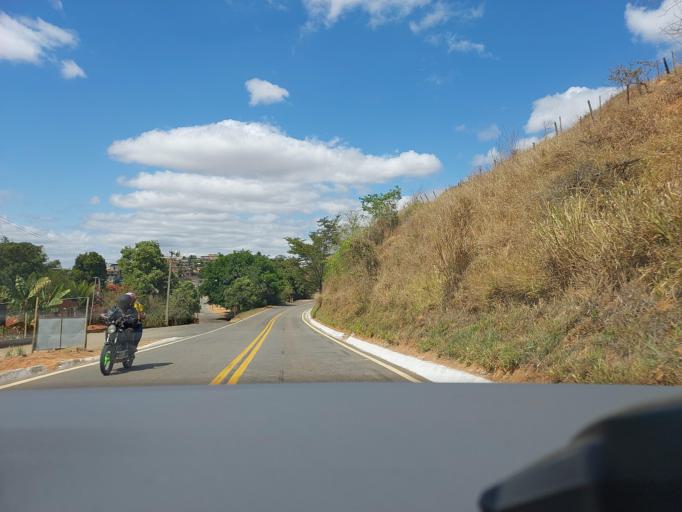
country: BR
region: Minas Gerais
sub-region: Muriae
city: Muriae
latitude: -21.1054
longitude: -42.4578
